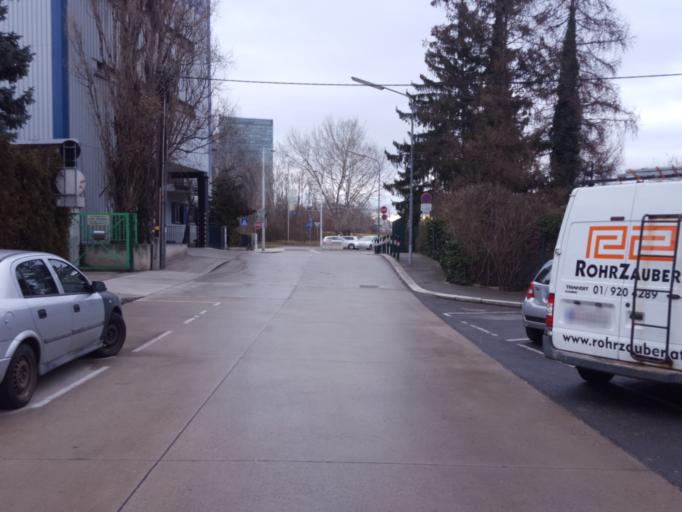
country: AT
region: Lower Austria
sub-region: Politischer Bezirk Modling
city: Vosendorf
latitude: 48.1682
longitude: 16.3346
